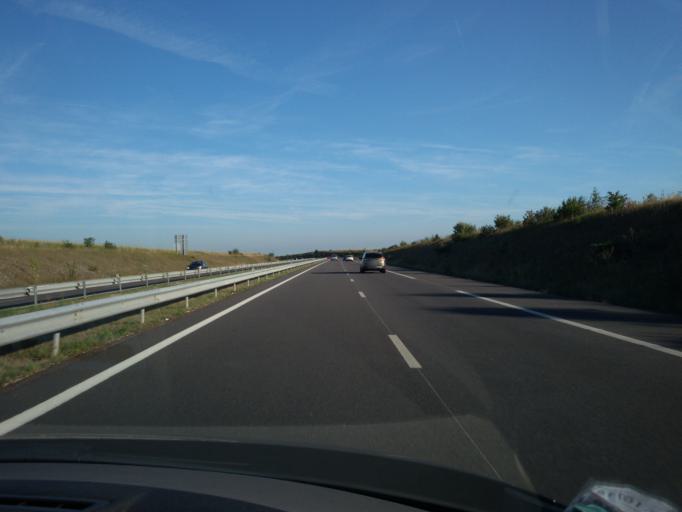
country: FR
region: Centre
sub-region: Departement du Cher
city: Plaimpied-Givaudins
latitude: 46.9928
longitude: 2.4083
